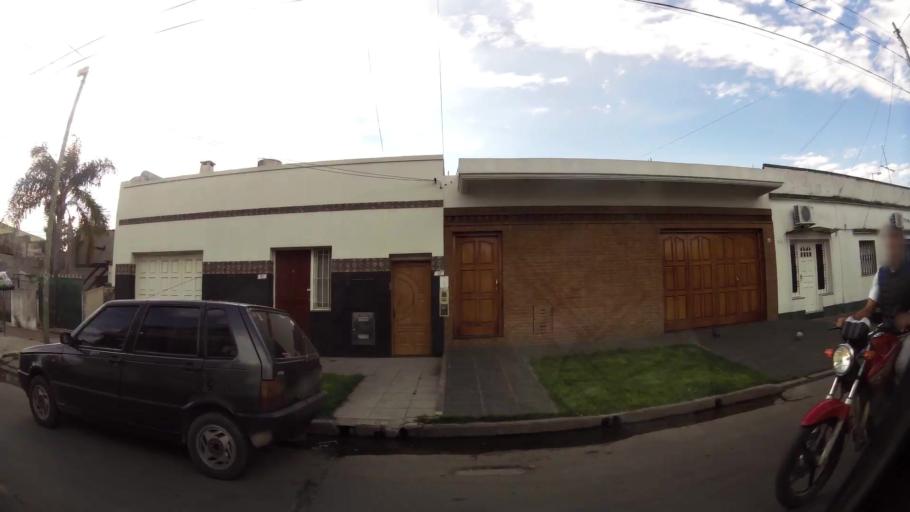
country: AR
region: Buenos Aires
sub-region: Partido de Avellaneda
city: Avellaneda
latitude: -34.6894
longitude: -58.3647
